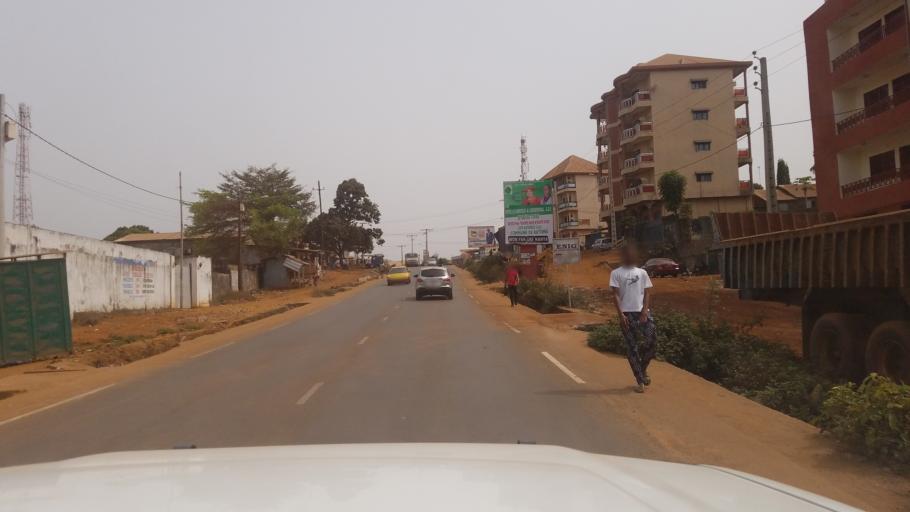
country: GN
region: Kindia
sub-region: Prefecture de Dubreka
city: Dubreka
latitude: 9.6631
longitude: -13.5941
